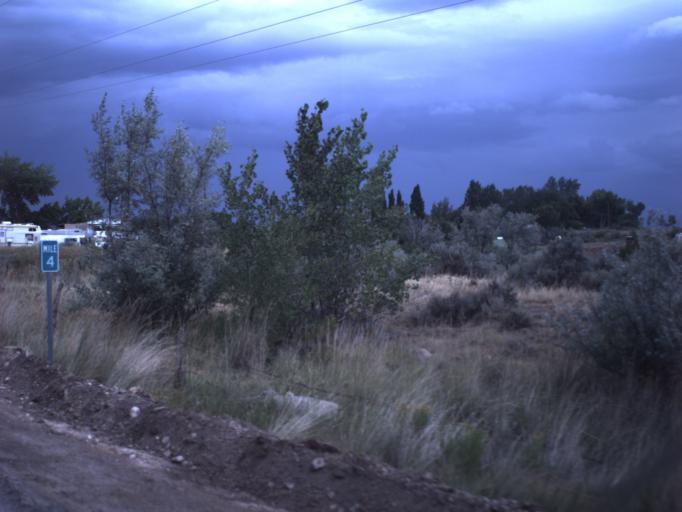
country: US
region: Utah
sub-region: Duchesne County
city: Roosevelt
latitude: 40.3462
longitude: -110.0277
